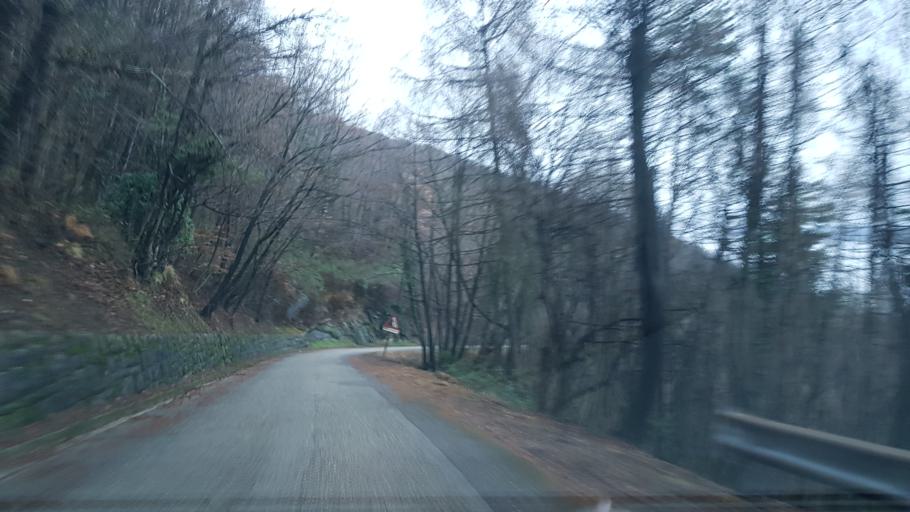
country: IT
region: Friuli Venezia Giulia
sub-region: Provincia di Udine
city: San Leonardo
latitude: 46.0968
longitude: 13.5445
